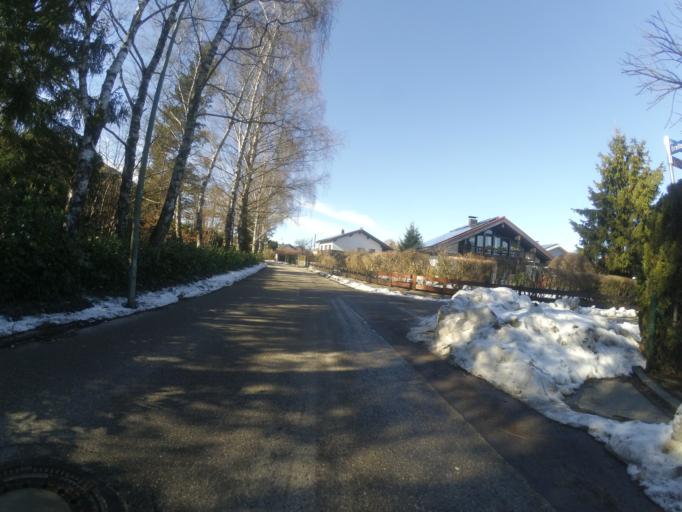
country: DE
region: Bavaria
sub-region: Upper Bavaria
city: Feldkirchen-Westerham
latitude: 47.8924
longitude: 11.8593
